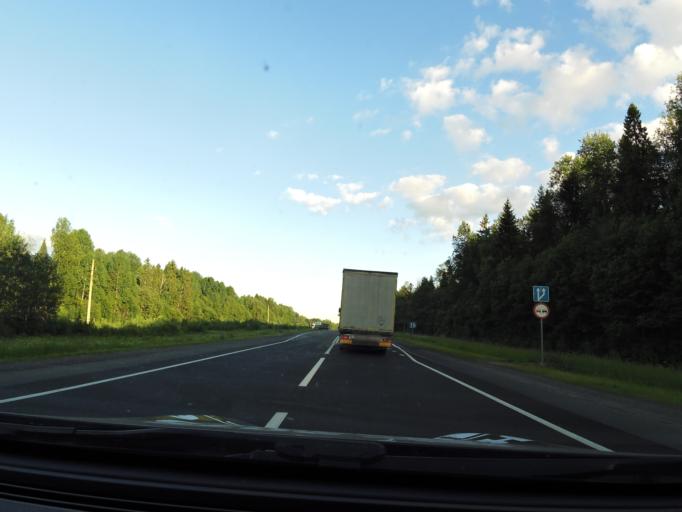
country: RU
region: Vologda
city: Gryazovets
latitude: 58.9793
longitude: 40.1464
